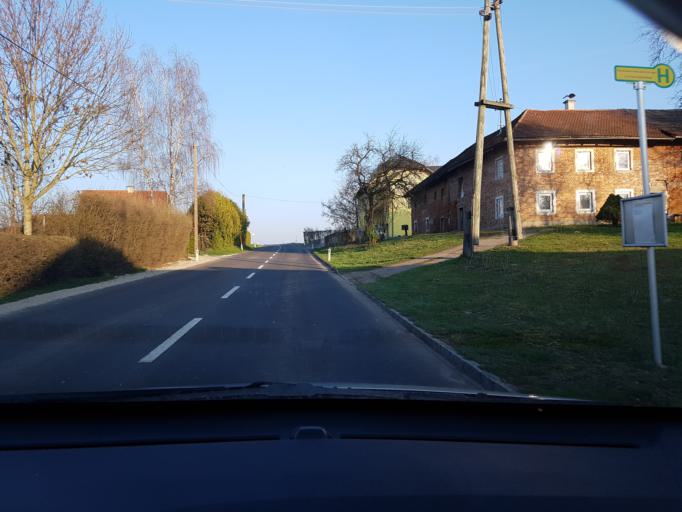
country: AT
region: Upper Austria
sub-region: Politischer Bezirk Linz-Land
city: Ansfelden
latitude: 48.1641
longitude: 14.3214
